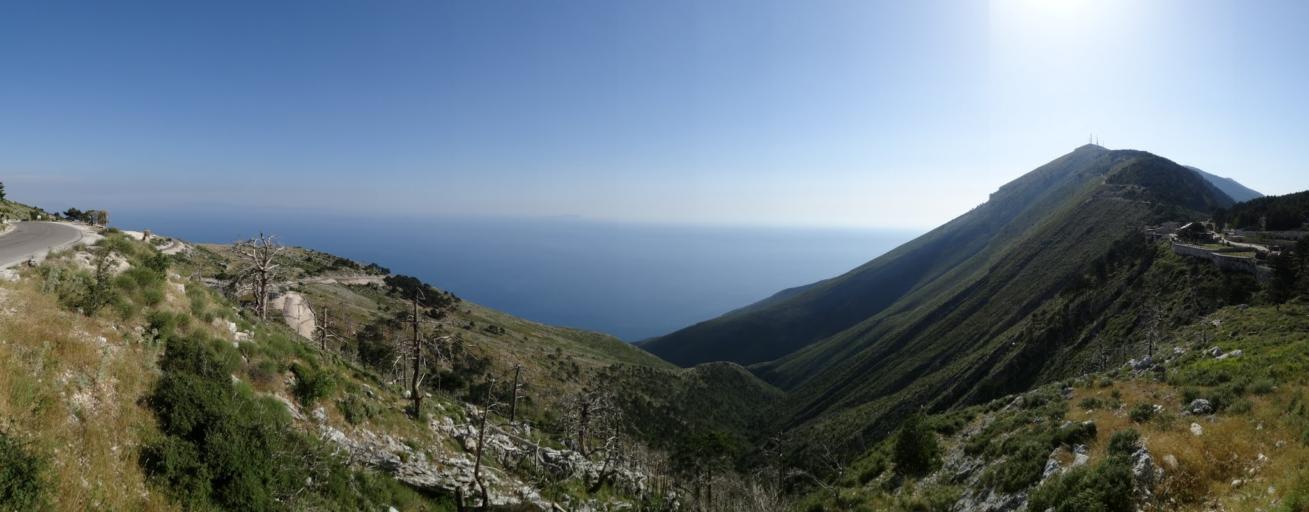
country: AL
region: Vlore
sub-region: Rrethi i Vlores
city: Vranisht
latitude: 40.1958
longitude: 19.5985
